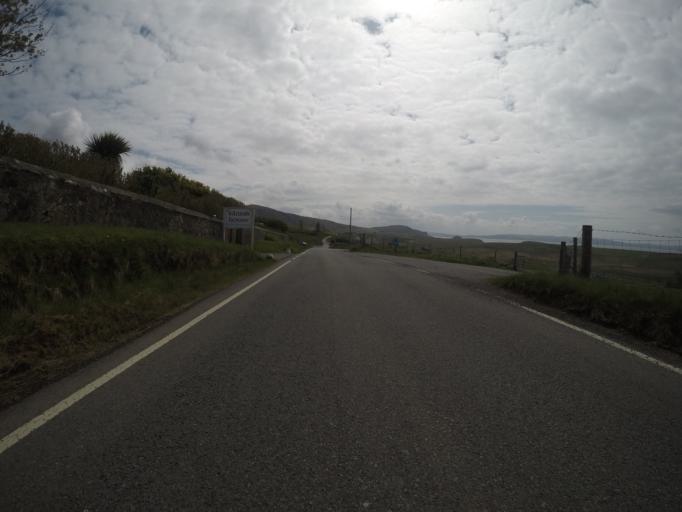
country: GB
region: Scotland
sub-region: Highland
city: Portree
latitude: 57.6297
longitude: -6.3784
